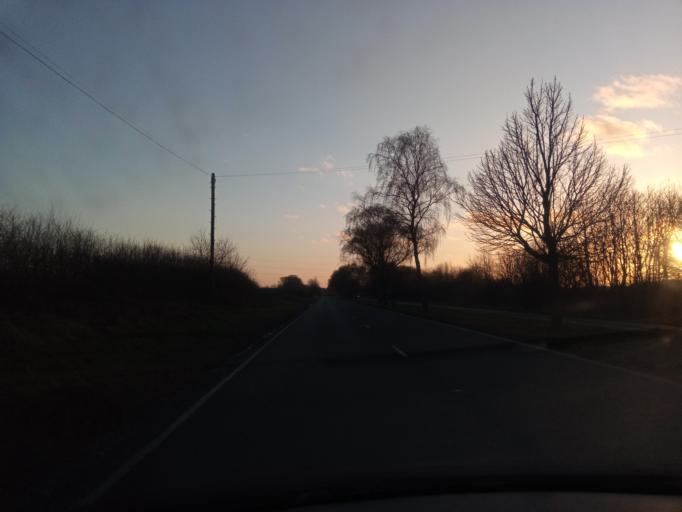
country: GB
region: England
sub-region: Nottinghamshire
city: Farnsfield
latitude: 53.0722
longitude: -1.0692
